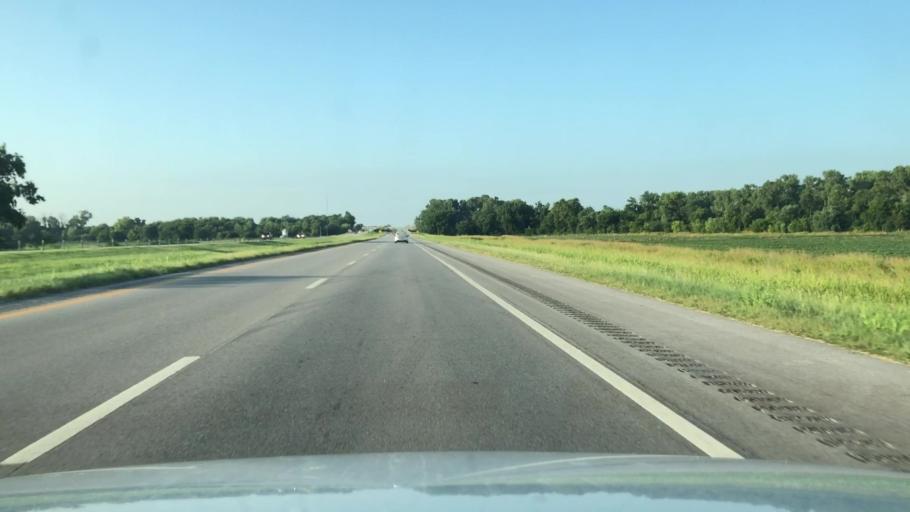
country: US
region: Oklahoma
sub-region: Washington County
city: Bartlesville
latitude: 36.6474
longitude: -95.9356
